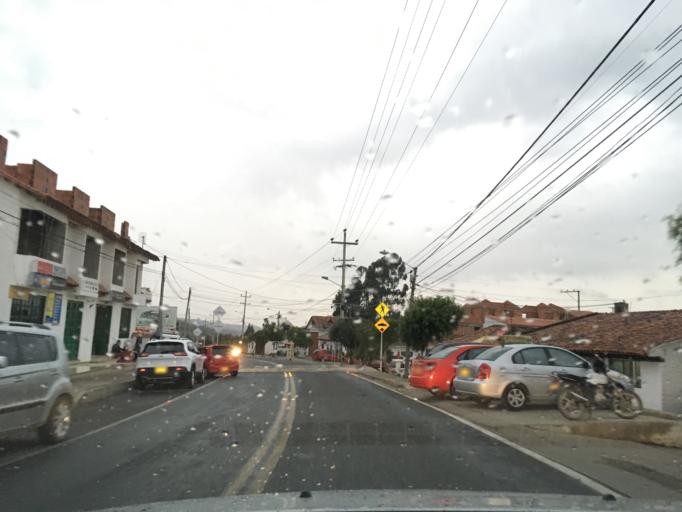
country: CO
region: Cundinamarca
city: Guatavita
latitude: 4.9338
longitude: -73.8320
